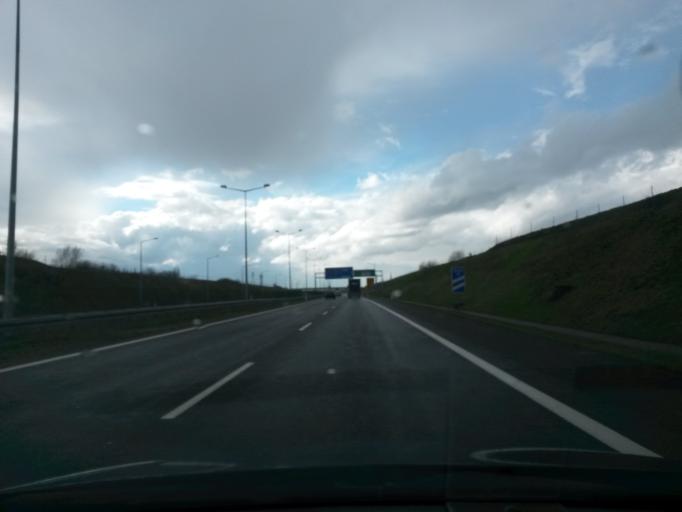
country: PL
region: Greater Poland Voivodeship
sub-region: Powiat poznanski
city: Daszewice
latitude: 52.3442
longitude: 17.0161
